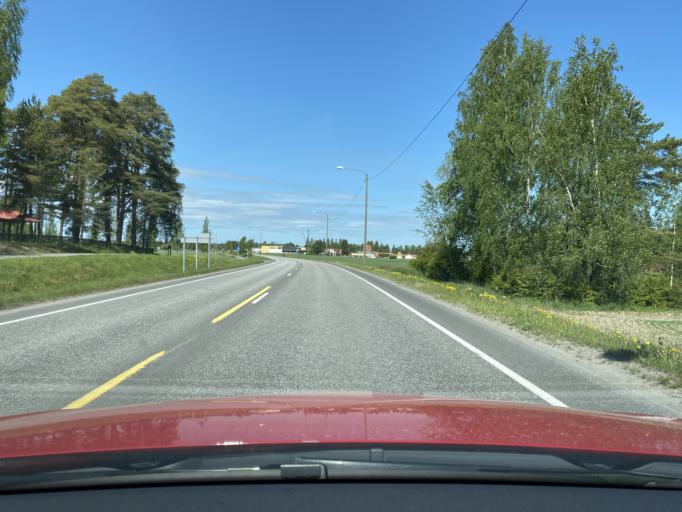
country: FI
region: Satakunta
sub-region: Rauma
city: Eura
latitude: 61.1171
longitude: 22.1439
